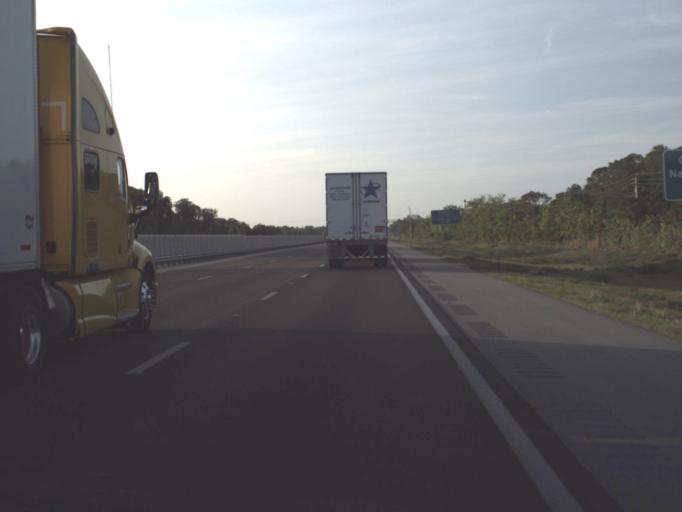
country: US
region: Florida
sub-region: Brevard County
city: Mims
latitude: 28.6487
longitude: -80.8624
